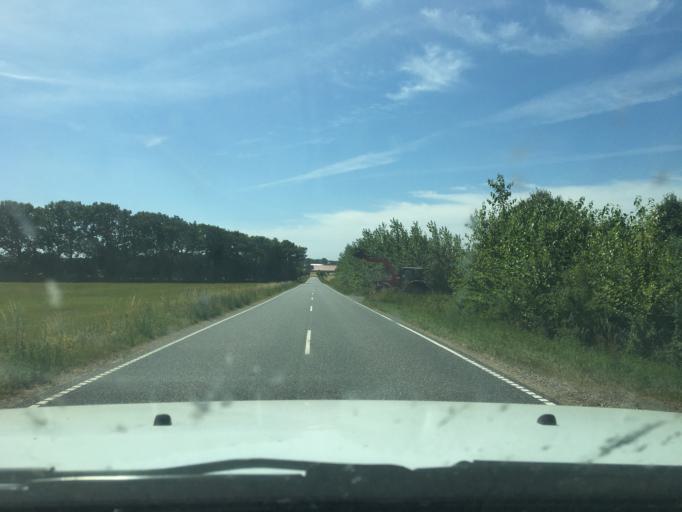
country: DK
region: Central Jutland
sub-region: Viborg Kommune
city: Bjerringbro
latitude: 56.5175
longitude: 9.6278
